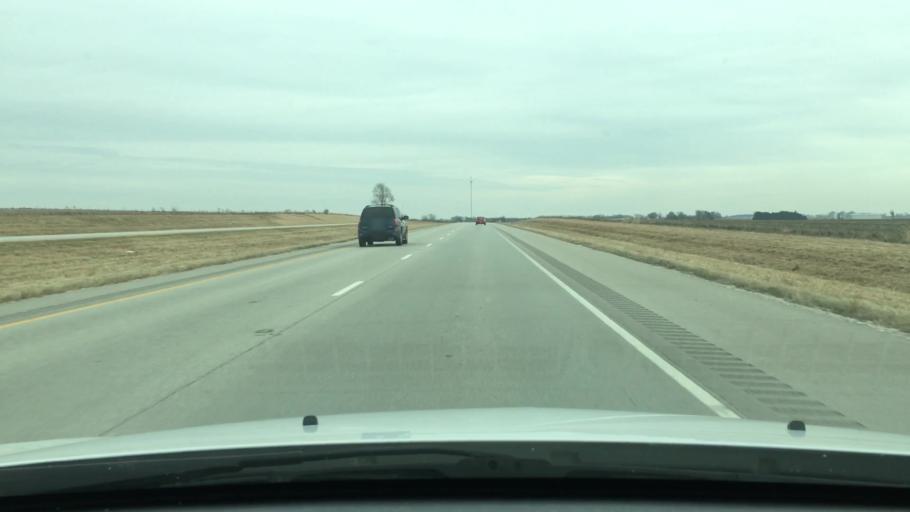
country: US
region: Illinois
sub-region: Morgan County
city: Jacksonville
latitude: 39.7382
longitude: -90.0978
